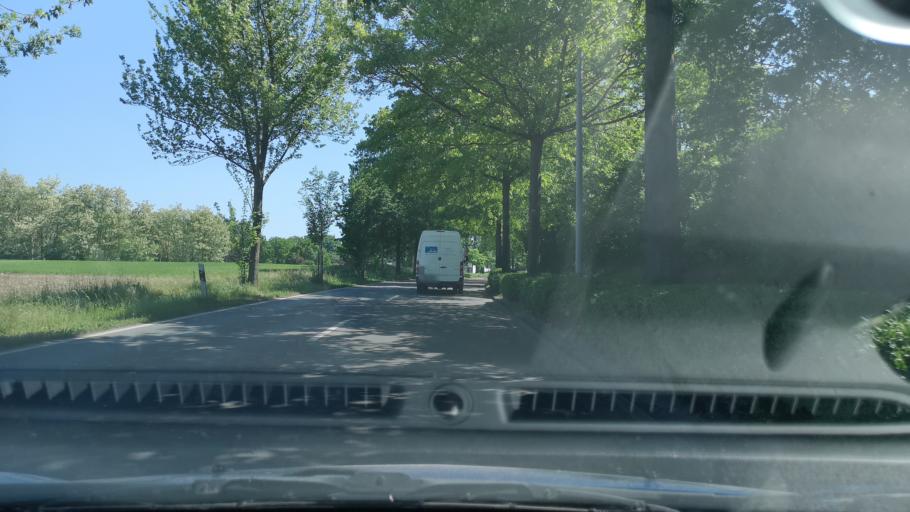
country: DE
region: Lower Saxony
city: Garbsen-Mitte
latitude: 52.4420
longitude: 9.6190
